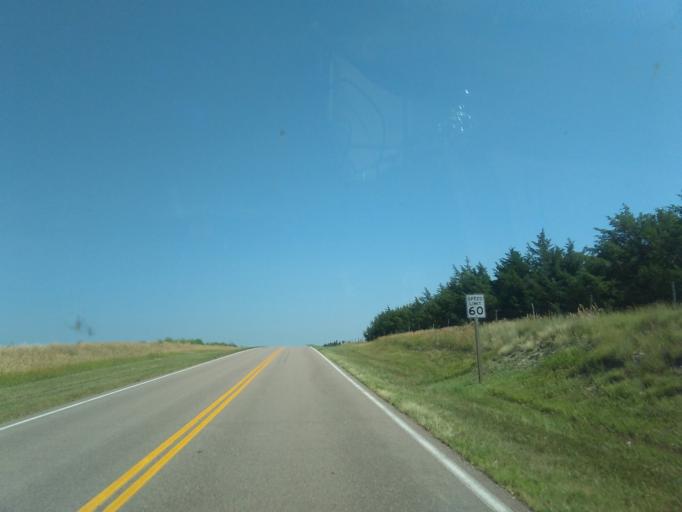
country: US
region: Nebraska
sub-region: Dundy County
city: Benkelman
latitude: 39.9036
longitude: -101.5411
